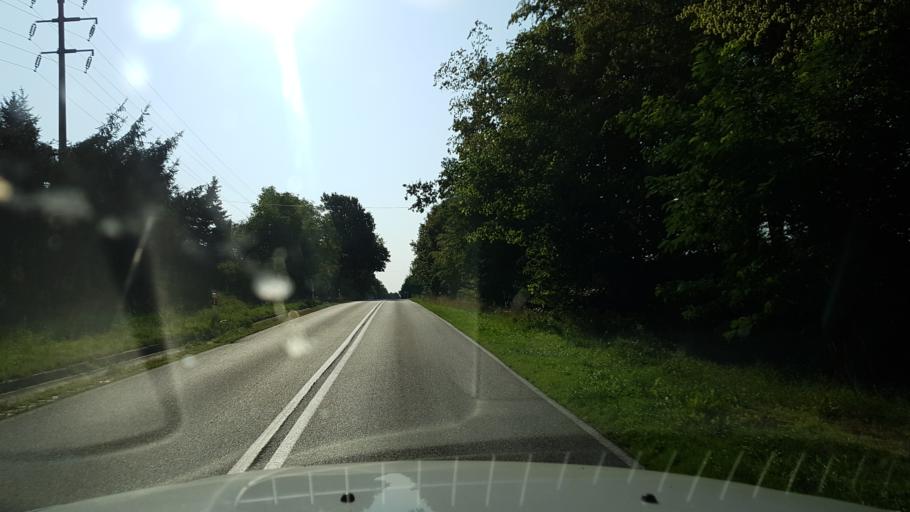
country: PL
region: West Pomeranian Voivodeship
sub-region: Powiat gryficki
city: Ploty
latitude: 53.7983
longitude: 15.2731
